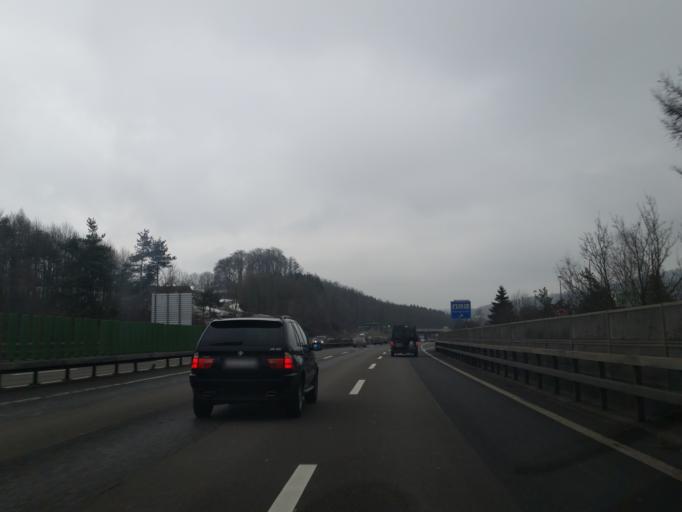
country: CH
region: Zurich
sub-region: Bezirk Pfaeffikon
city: Effretikon / Watt
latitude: 47.4476
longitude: 8.6980
